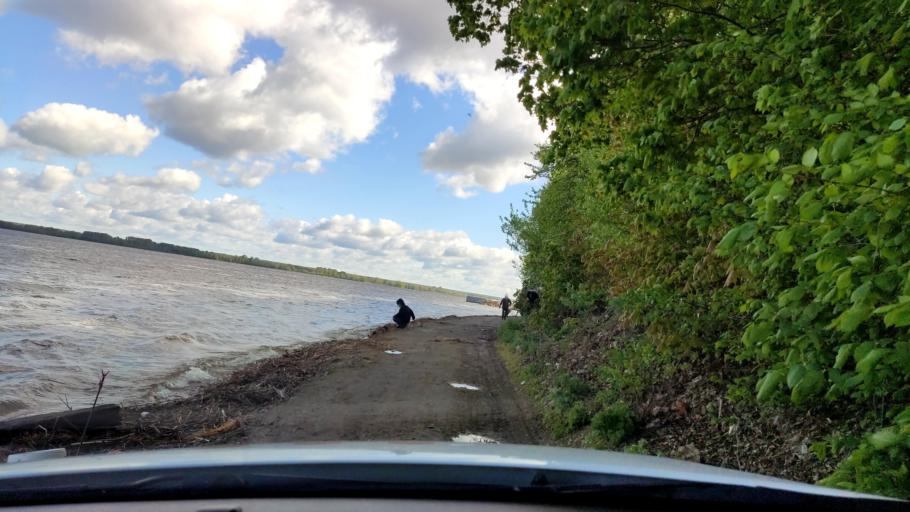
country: RU
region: Tatarstan
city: Sviyazhsk
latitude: 55.7804
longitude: 48.6967
